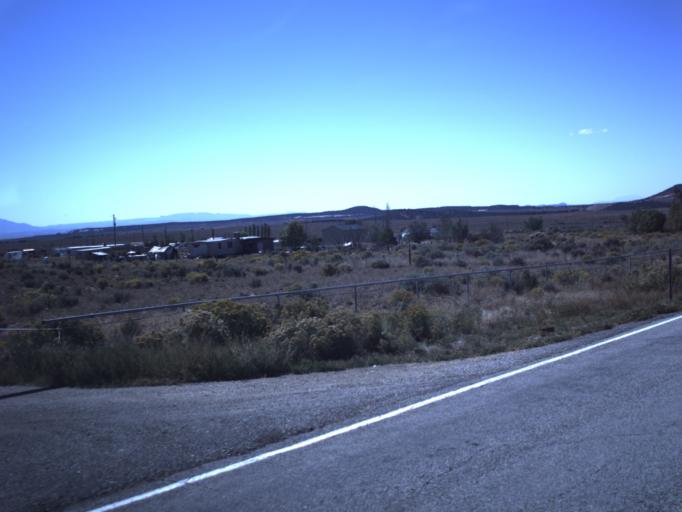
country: US
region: Utah
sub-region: Grand County
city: Moab
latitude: 38.3094
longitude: -109.2898
